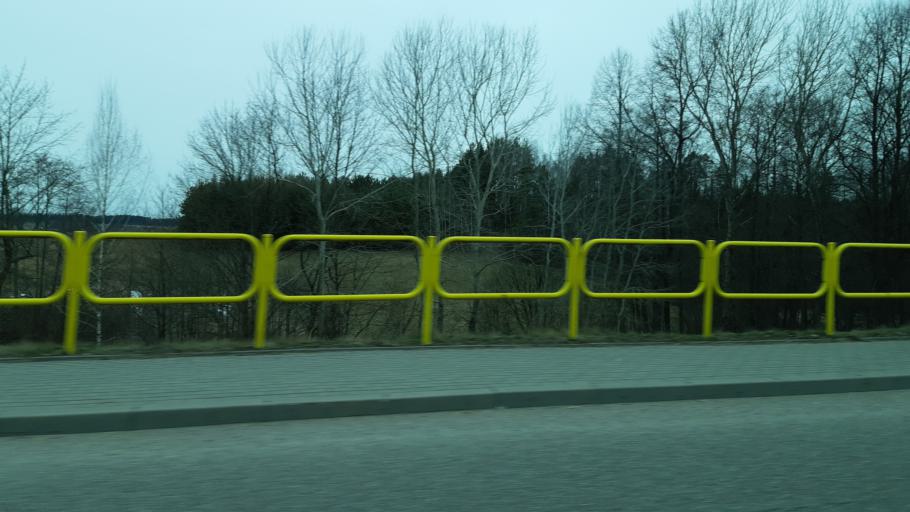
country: PL
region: Podlasie
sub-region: Suwalki
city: Suwalki
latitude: 54.3183
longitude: 22.9639
